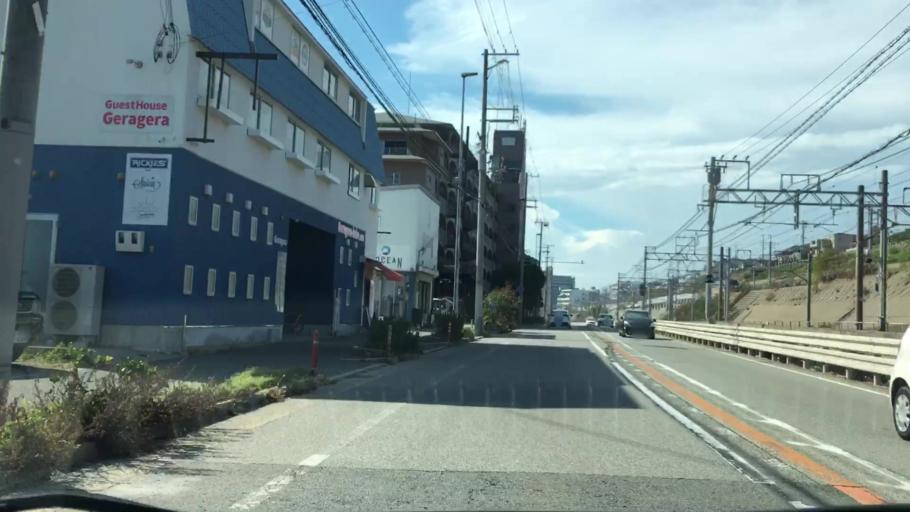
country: JP
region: Hyogo
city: Akashi
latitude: 34.6404
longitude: 135.0245
